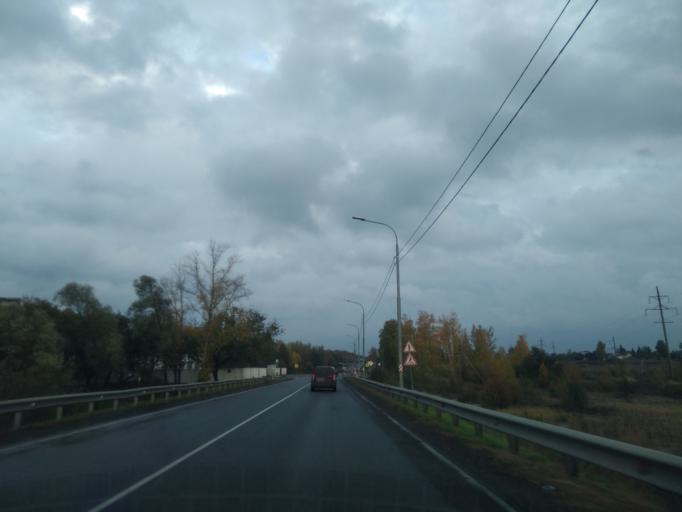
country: RU
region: Lipetsk
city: Syrskoye
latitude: 52.6033
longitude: 39.3553
